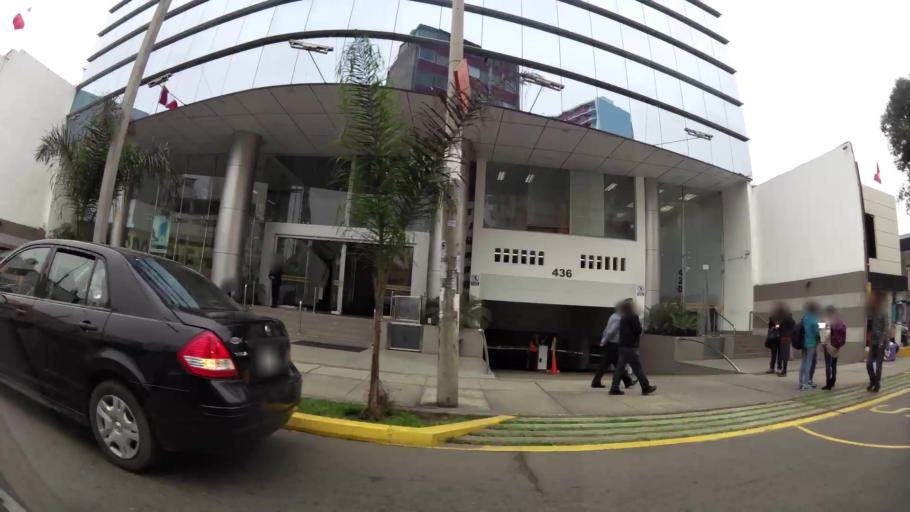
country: PE
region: Lima
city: Lima
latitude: -12.0690
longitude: -77.0380
